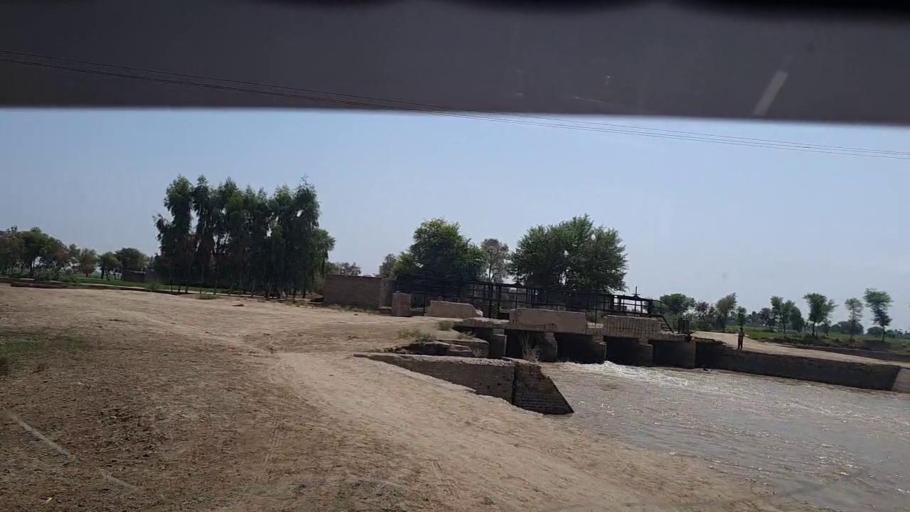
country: PK
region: Sindh
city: Tangwani
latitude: 28.2261
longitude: 68.9027
